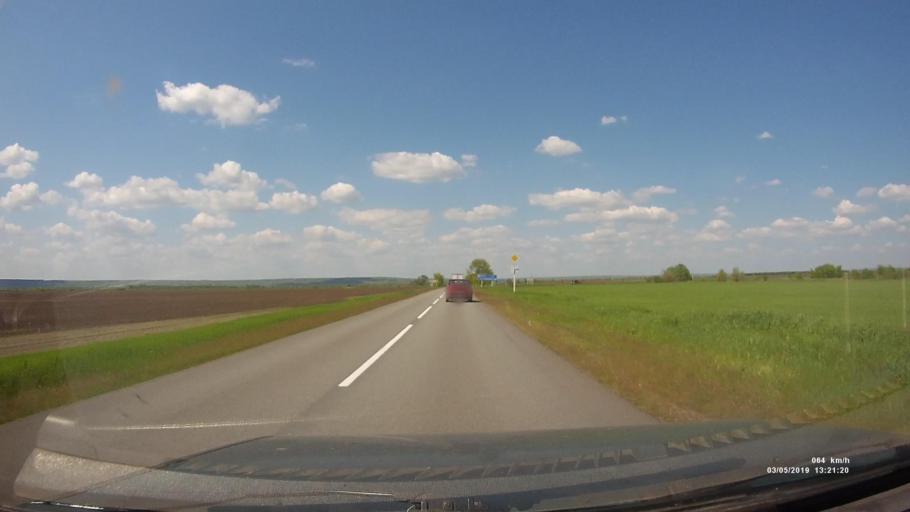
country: RU
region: Rostov
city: Semikarakorsk
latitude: 47.5541
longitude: 40.7476
